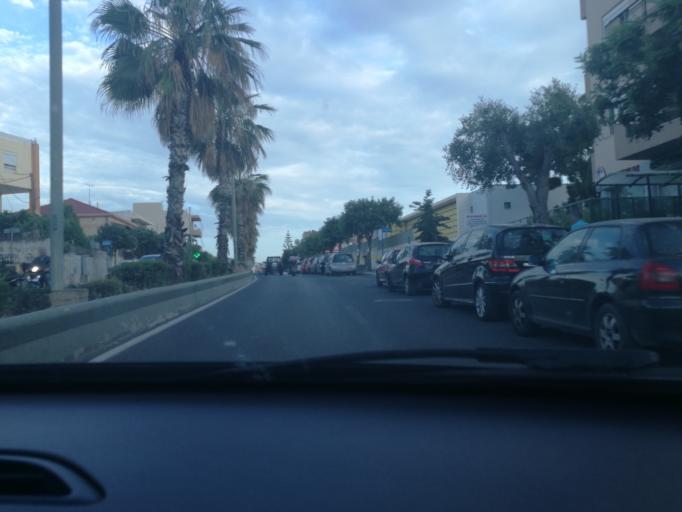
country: GR
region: Crete
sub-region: Nomos Irakleiou
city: Irakleion
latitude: 35.3171
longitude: 25.1457
